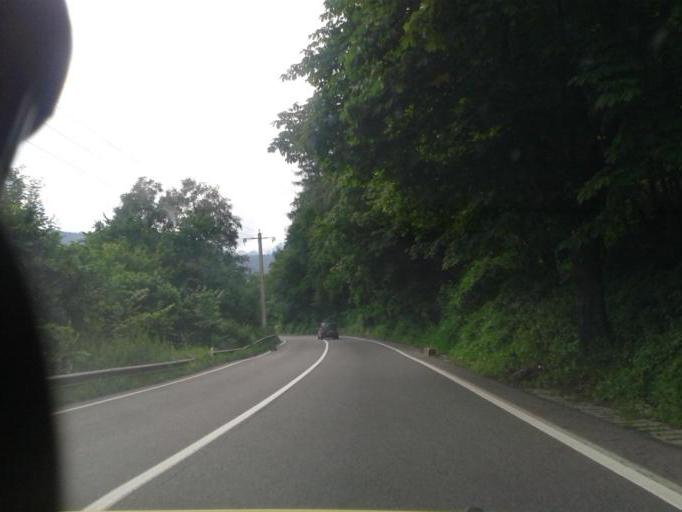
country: RO
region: Prahova
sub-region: Comuna Comarnic
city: Posada
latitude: 45.2987
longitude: 25.5921
